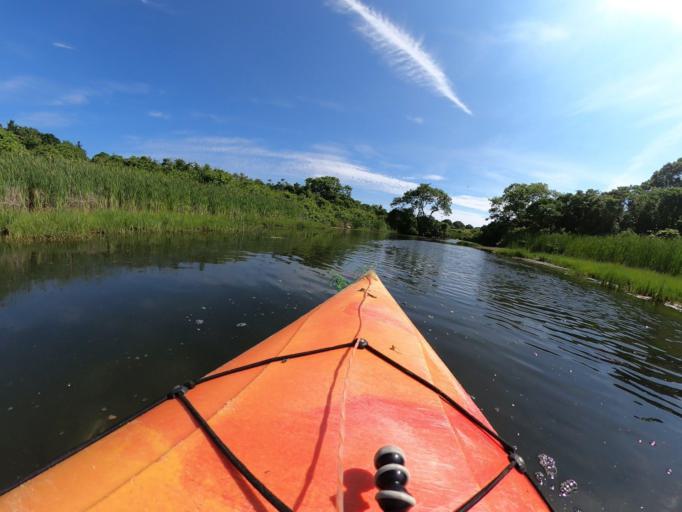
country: US
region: Massachusetts
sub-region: Dukes County
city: West Tisbury
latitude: 41.3290
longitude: -70.7863
